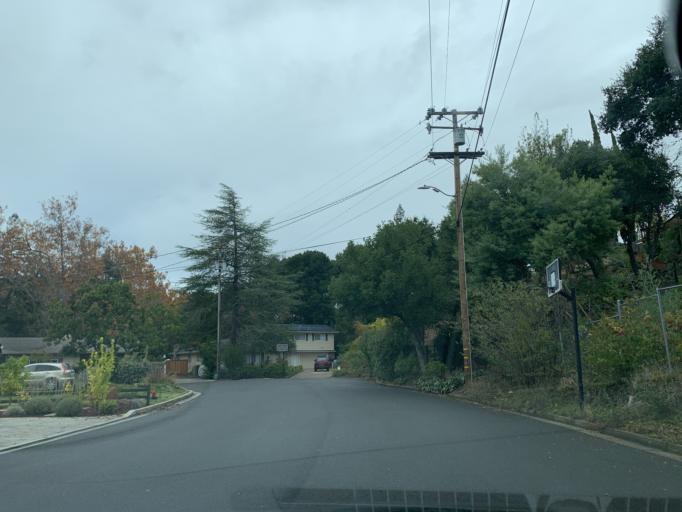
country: US
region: California
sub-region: Santa Clara County
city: Cupertino
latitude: 37.3303
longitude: -122.0601
